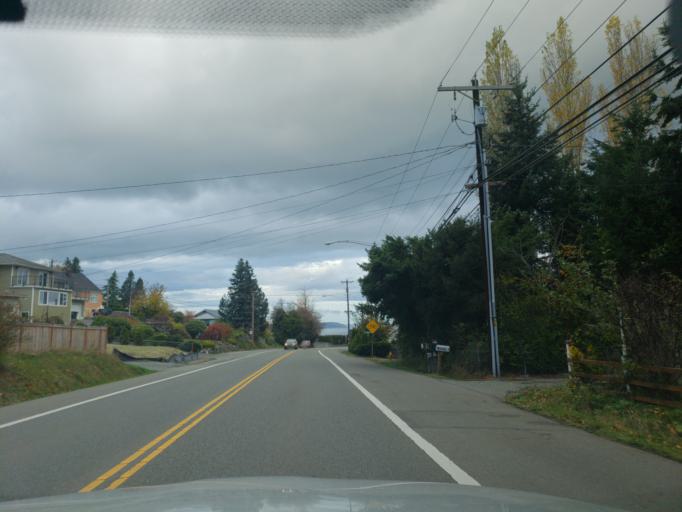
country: US
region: Washington
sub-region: Snohomish County
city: Everett
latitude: 47.9584
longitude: -122.2421
